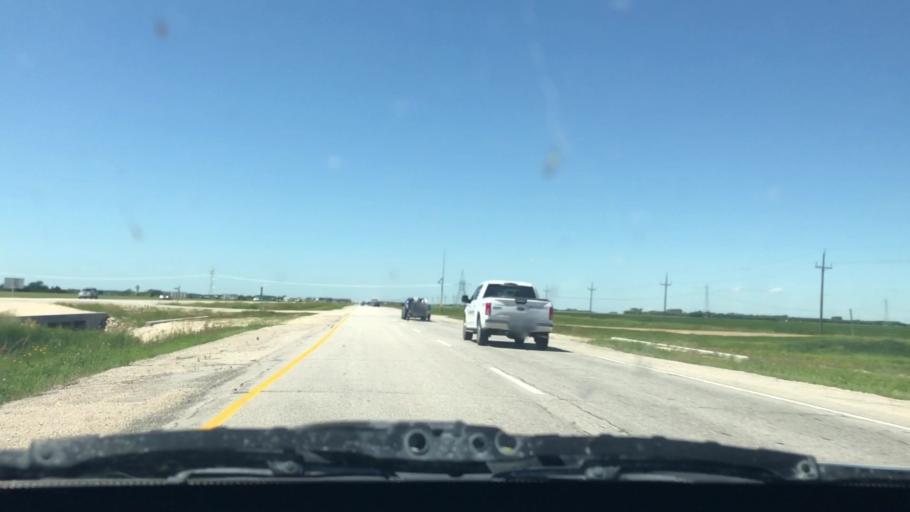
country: CA
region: Manitoba
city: Steinbach
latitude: 49.7079
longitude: -96.6627
